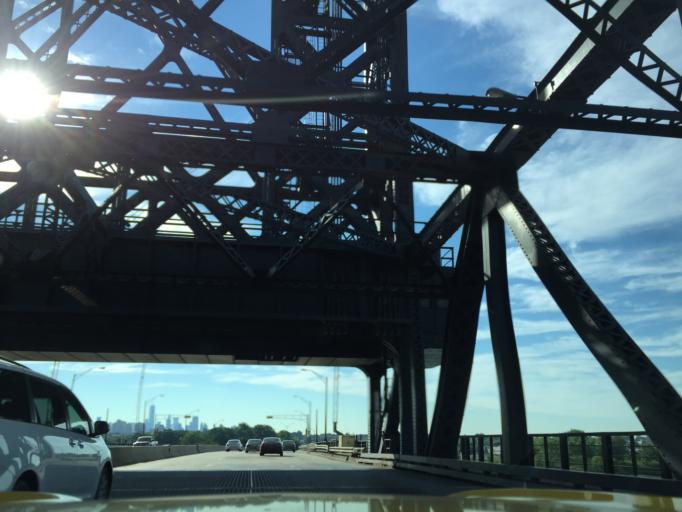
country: US
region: New Jersey
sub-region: Hudson County
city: Jersey City
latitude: 40.7273
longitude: -74.0992
